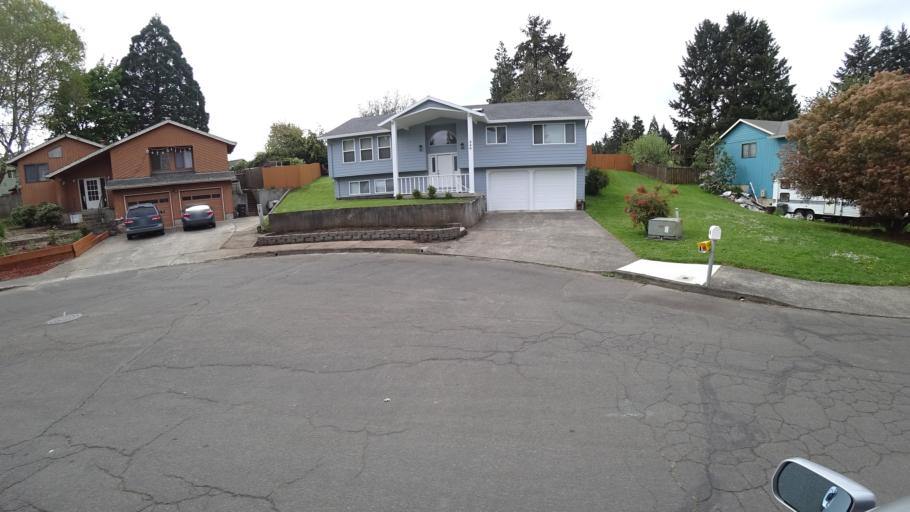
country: US
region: Oregon
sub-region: Washington County
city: Hillsboro
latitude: 45.5263
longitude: -122.9985
